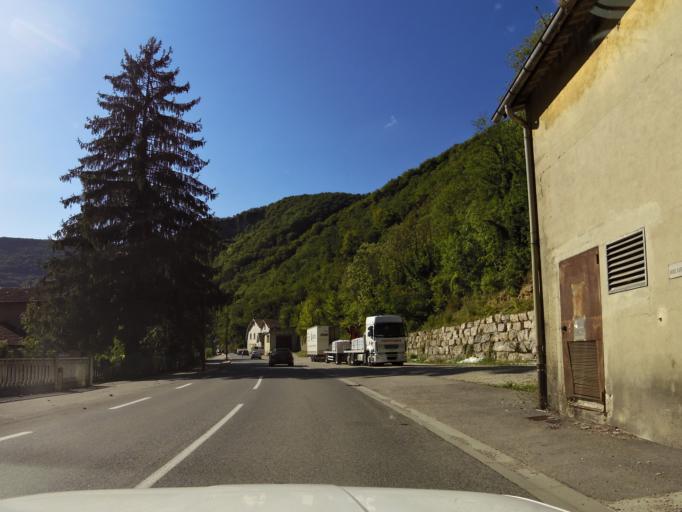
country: FR
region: Rhone-Alpes
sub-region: Departement de l'Ain
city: Saint-Rambert-en-Bugey
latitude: 45.9504
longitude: 5.4511
